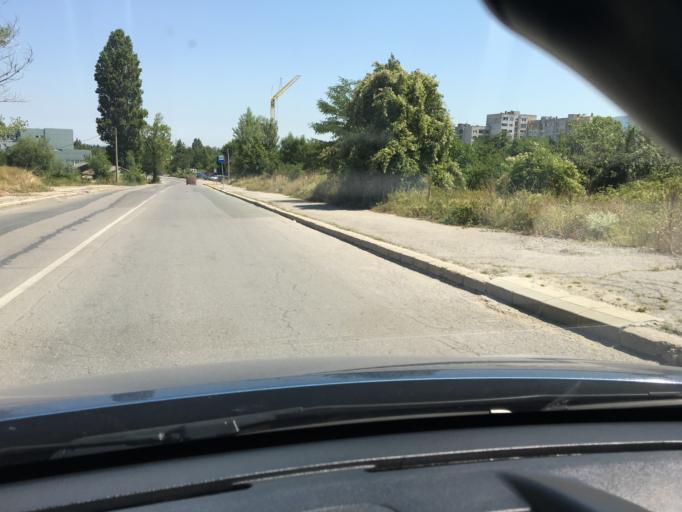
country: BG
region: Sofia-Capital
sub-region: Stolichna Obshtina
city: Sofia
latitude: 42.6369
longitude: 23.3986
